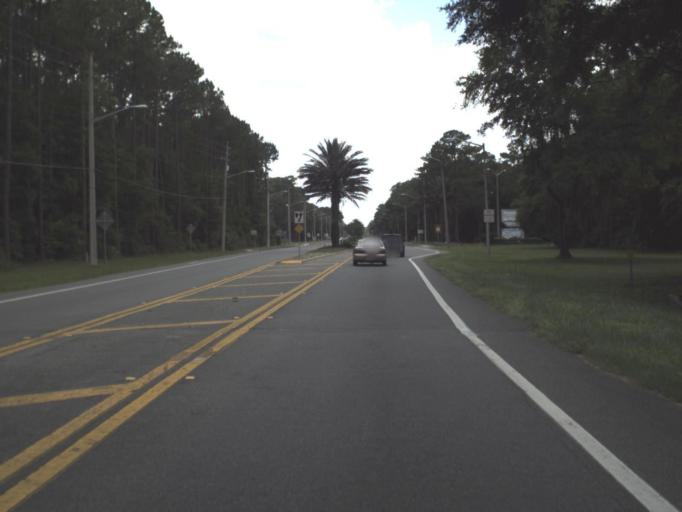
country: US
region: Florida
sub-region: Alachua County
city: Gainesville
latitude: 29.6778
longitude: -82.2753
